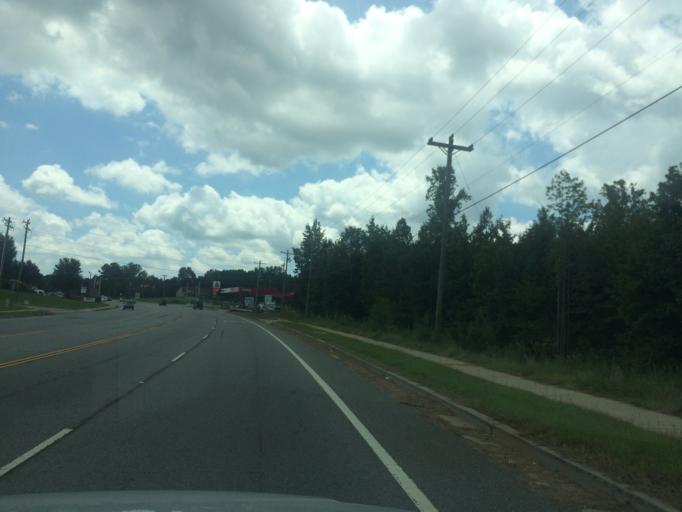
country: US
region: South Carolina
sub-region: Spartanburg County
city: Inman
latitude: 35.0932
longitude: -82.0401
